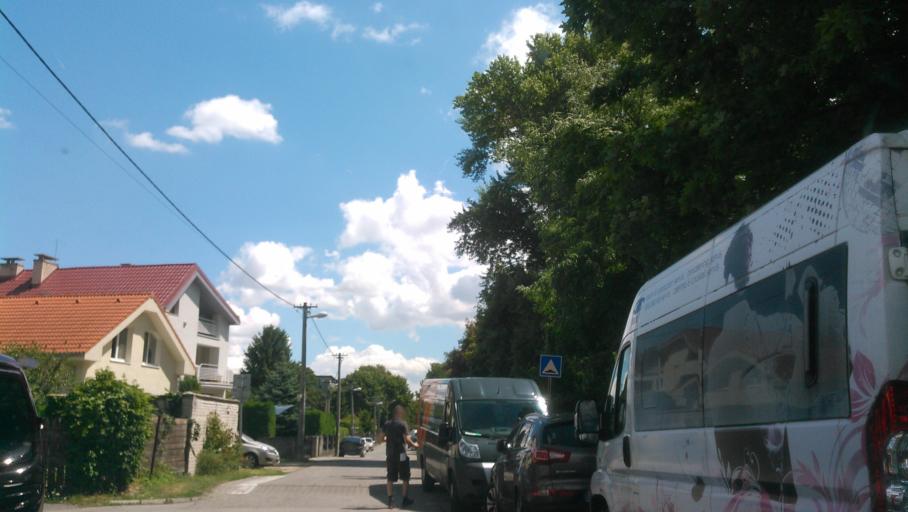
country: SK
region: Bratislavsky
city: Bratislava
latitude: 48.1252
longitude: 17.0906
